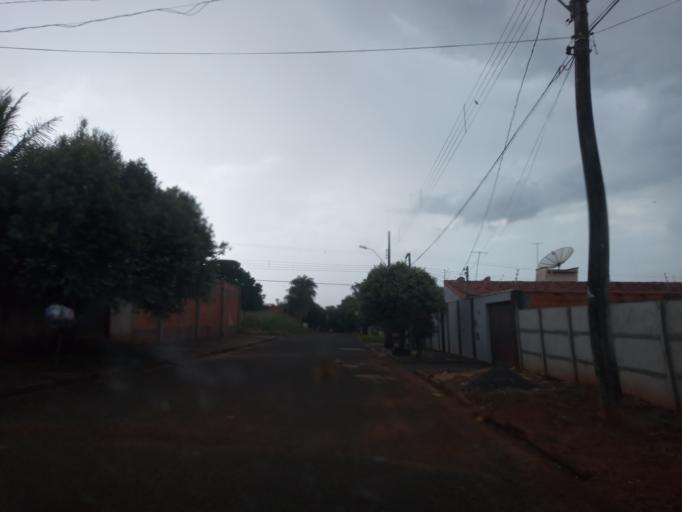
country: BR
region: Minas Gerais
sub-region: Ituiutaba
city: Ituiutaba
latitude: -18.9857
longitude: -49.4439
